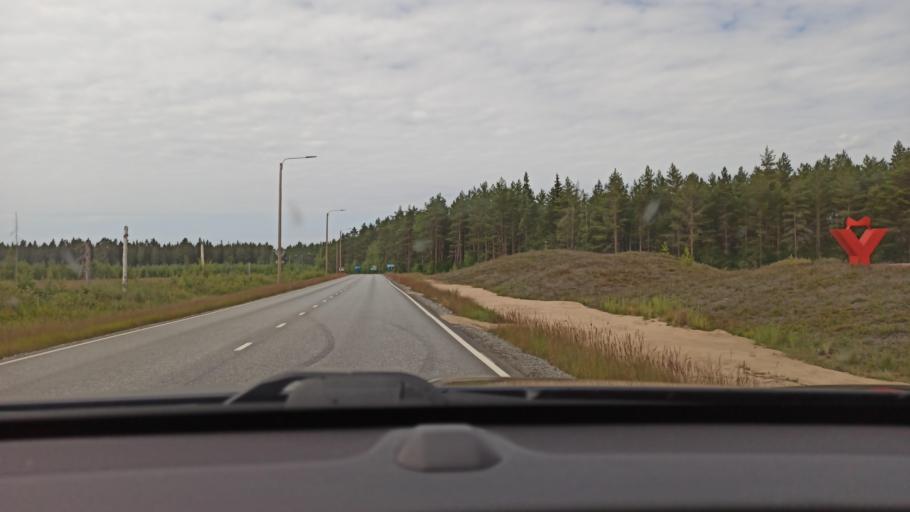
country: FI
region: Satakunta
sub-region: Pori
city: Luvia
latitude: 61.5707
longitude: 21.5520
